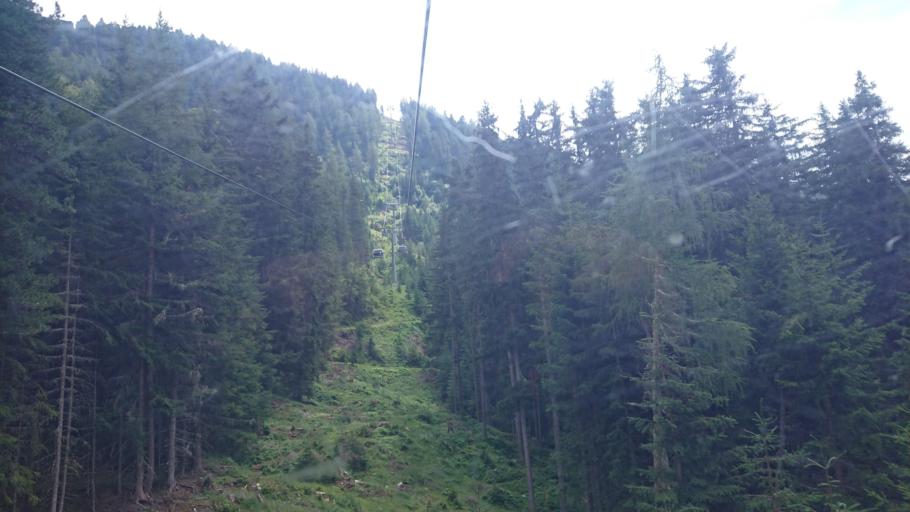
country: AT
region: Tyrol
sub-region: Politischer Bezirk Imst
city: Oetz
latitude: 47.2236
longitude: 10.9325
